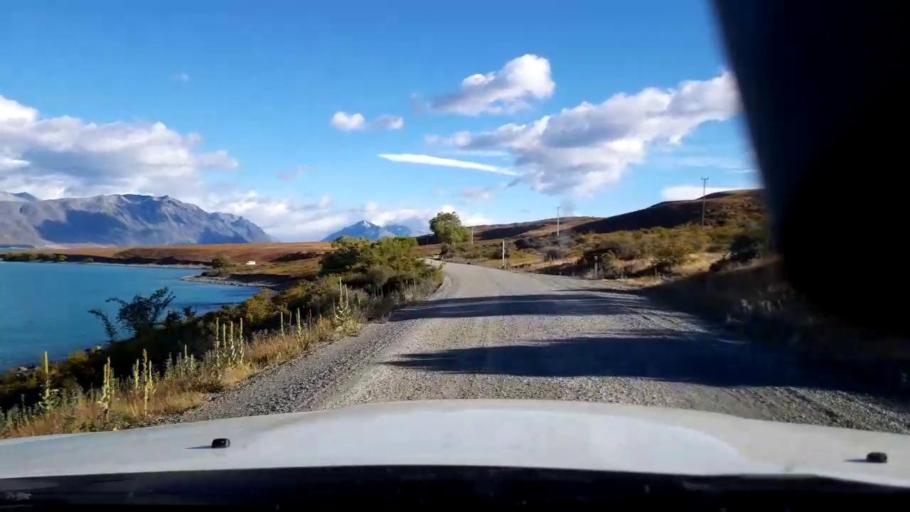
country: NZ
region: Canterbury
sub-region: Timaru District
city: Pleasant Point
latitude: -43.9288
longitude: 170.5603
